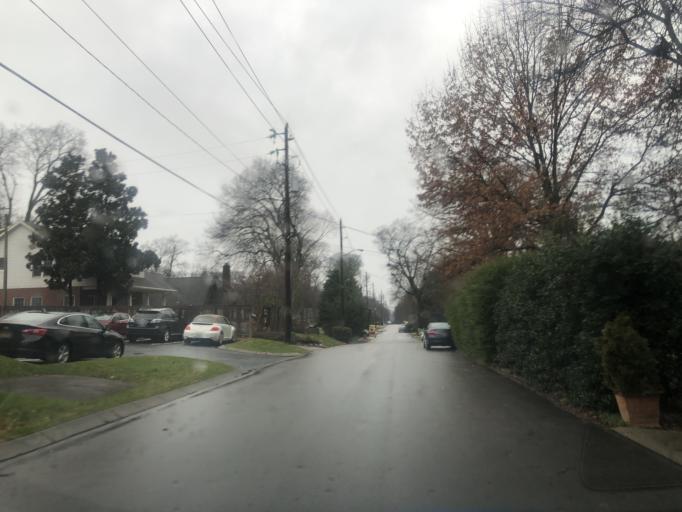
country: US
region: Tennessee
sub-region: Davidson County
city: Nashville
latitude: 36.1265
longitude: -86.8052
